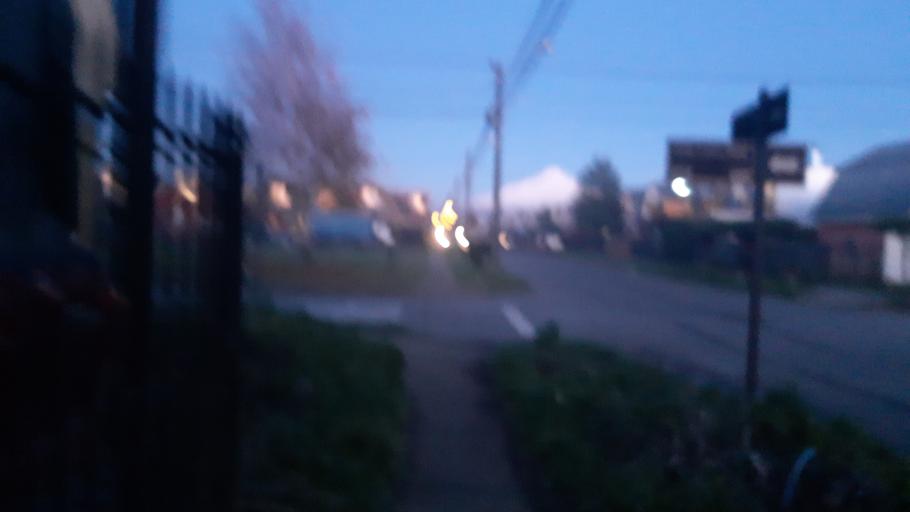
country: CL
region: Araucania
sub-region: Provincia de Cautin
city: Villarrica
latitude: -39.3085
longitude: -72.2156
